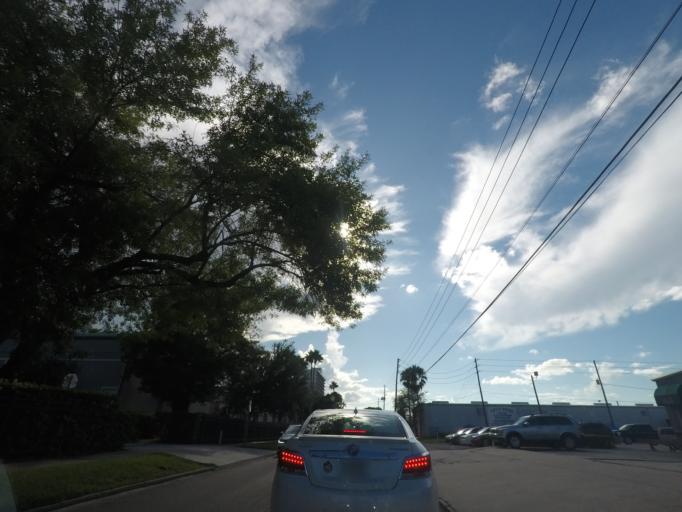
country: US
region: Florida
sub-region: Orange County
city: Fairview Shores
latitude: 28.5895
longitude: -81.3712
